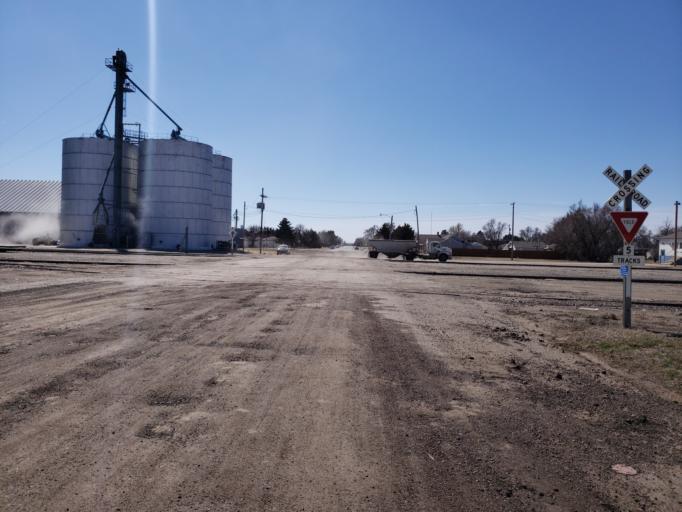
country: US
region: Kansas
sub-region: Ness County
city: Ness City
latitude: 38.4521
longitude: -99.9009
